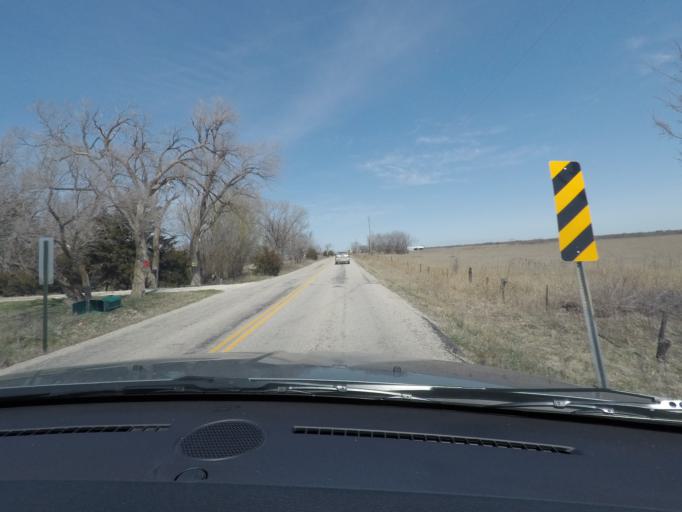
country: US
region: Kansas
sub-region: Lyon County
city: Emporia
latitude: 38.5539
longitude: -96.1699
